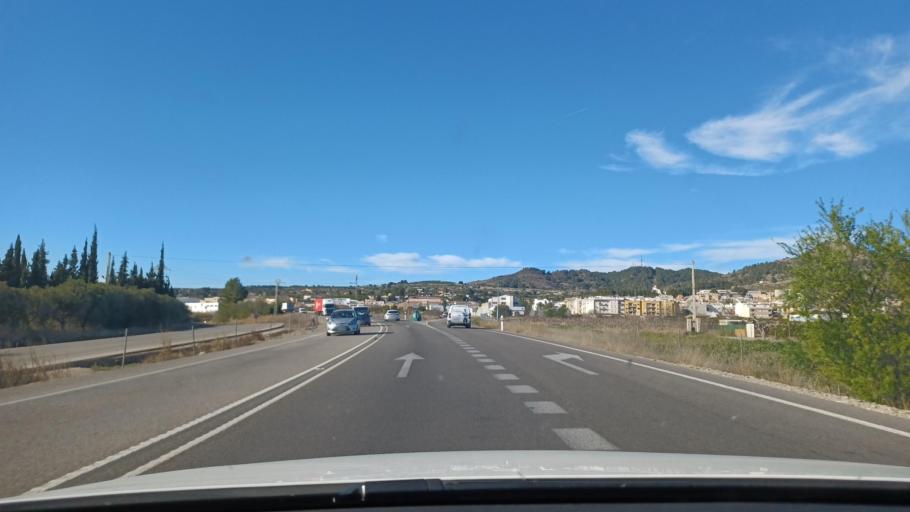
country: ES
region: Valencia
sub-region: Provincia de Valencia
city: Llosa de Ranes
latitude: 39.0113
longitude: -0.5335
